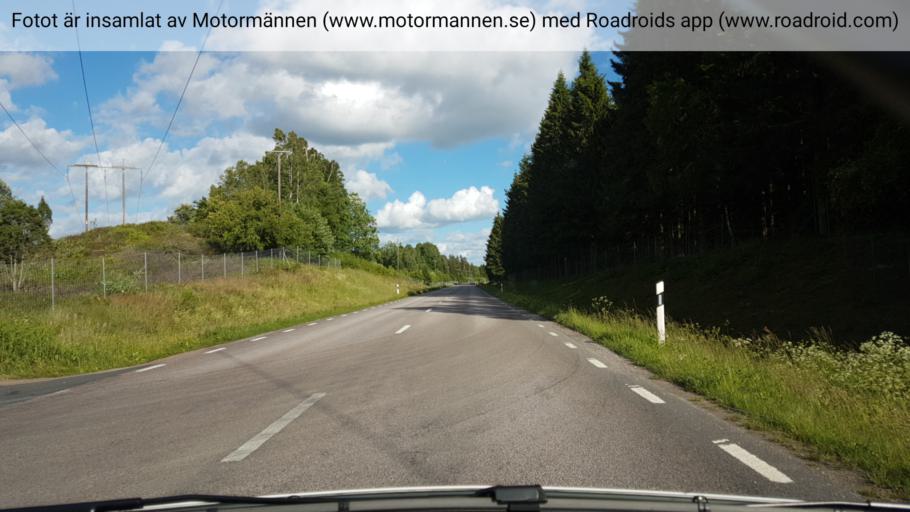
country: SE
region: Vaestra Goetaland
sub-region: Falkopings Kommun
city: Floby
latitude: 58.1790
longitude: 13.3813
